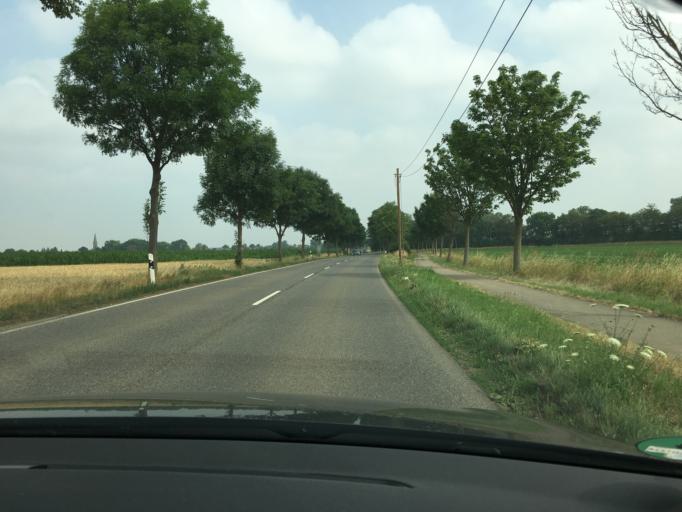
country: DE
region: North Rhine-Westphalia
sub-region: Regierungsbezirk Koln
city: Norvenich
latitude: 50.8024
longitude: 6.5865
